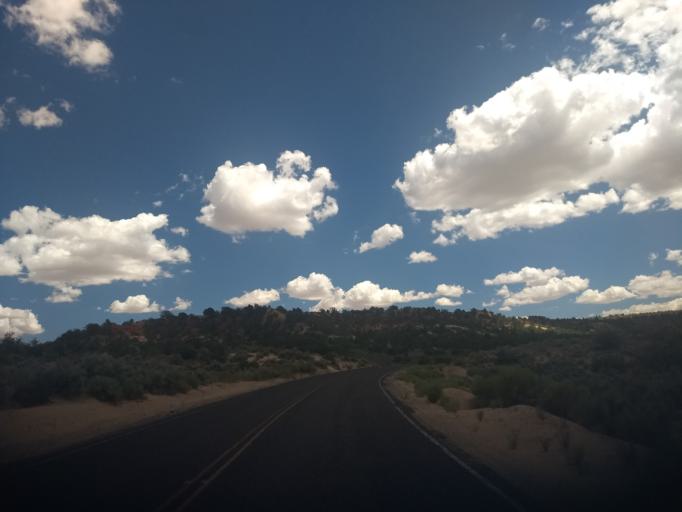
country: US
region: Utah
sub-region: Kane County
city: Kanab
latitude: 37.1210
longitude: -112.6769
